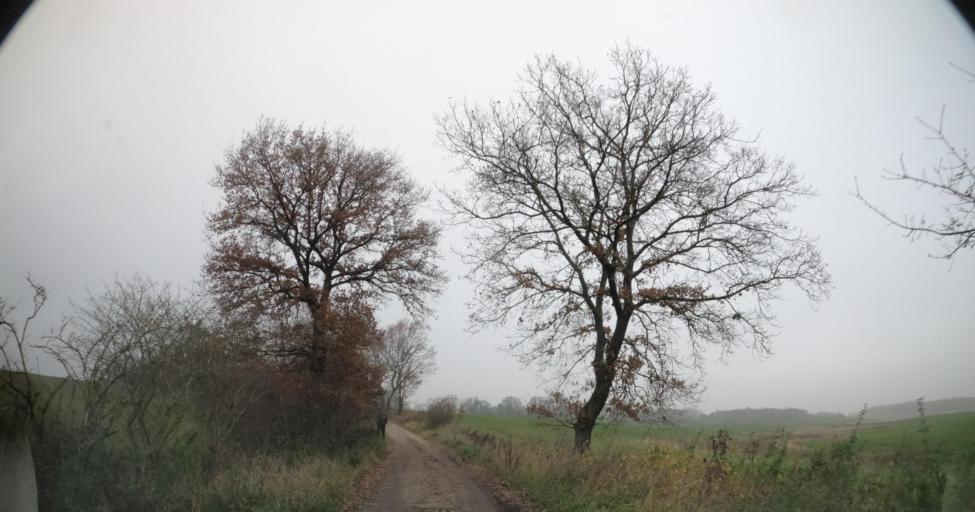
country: PL
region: West Pomeranian Voivodeship
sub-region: Powiat drawski
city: Drawsko Pomorskie
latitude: 53.5911
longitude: 15.7947
